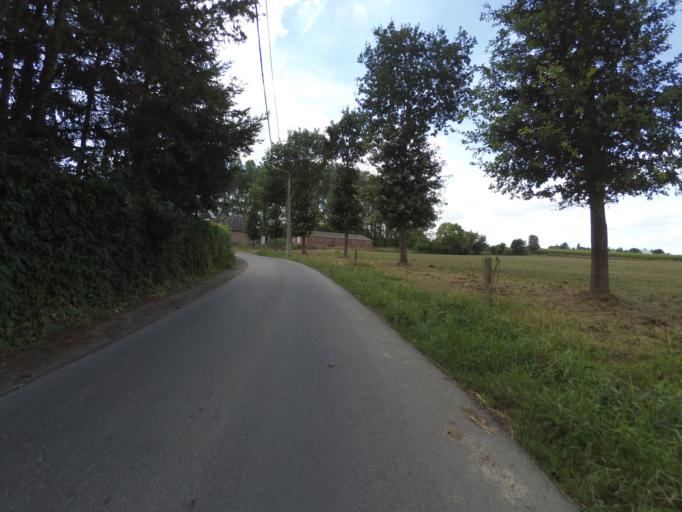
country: BE
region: Flanders
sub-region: Provincie Oost-Vlaanderen
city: Zottegem
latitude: 50.8607
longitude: 3.7651
